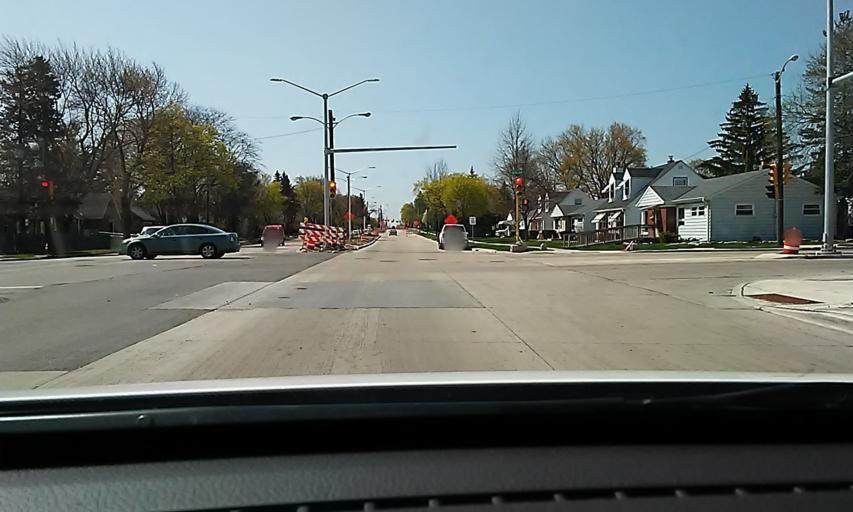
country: US
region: Wisconsin
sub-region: Milwaukee County
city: Greenfield
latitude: 42.9814
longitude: -87.9879
